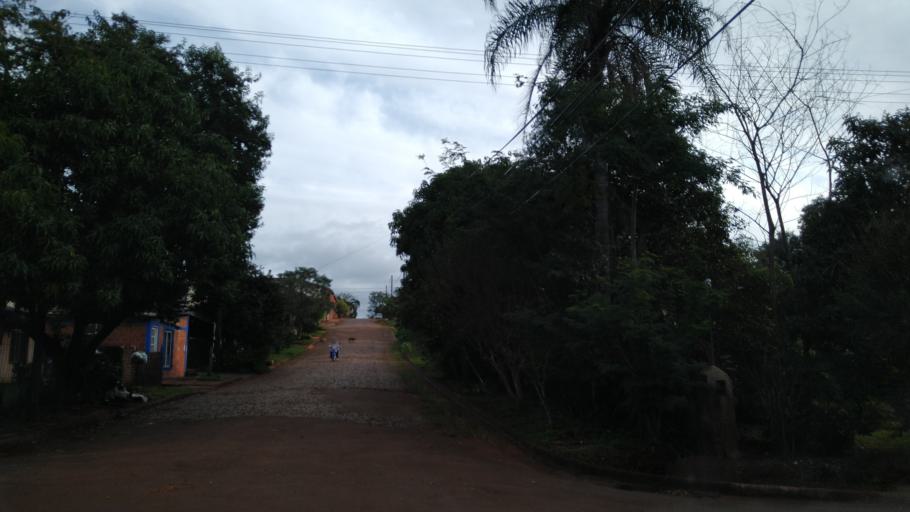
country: AR
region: Misiones
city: Jardin America
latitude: -27.0424
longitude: -55.2372
